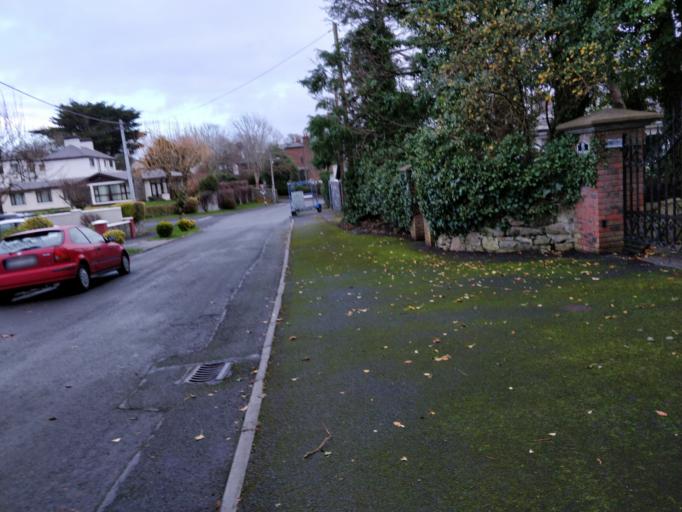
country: IE
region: Connaught
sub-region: County Galway
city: Gaillimh
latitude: 53.2596
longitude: -9.0884
